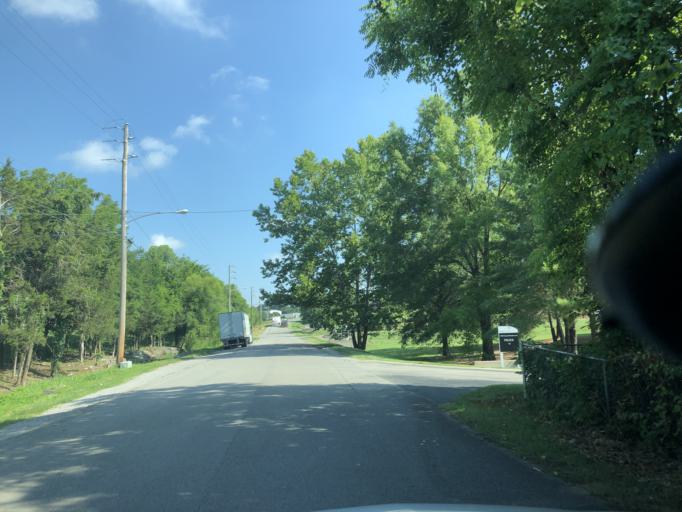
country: US
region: Tennessee
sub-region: Rutherford County
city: La Vergne
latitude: 36.0125
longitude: -86.6154
